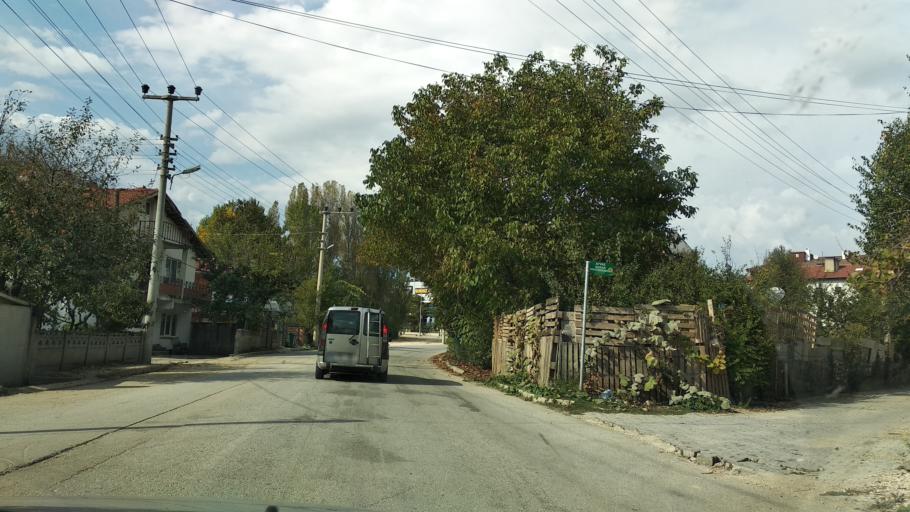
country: TR
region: Bolu
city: Bolu
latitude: 40.7294
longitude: 31.5863
